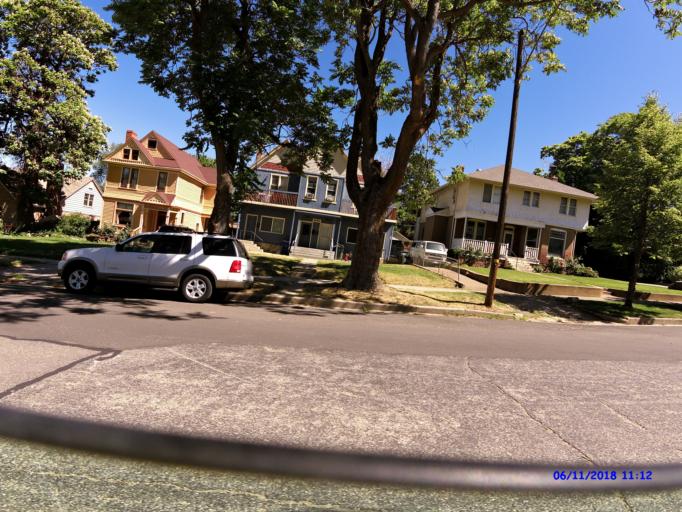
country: US
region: Utah
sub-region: Weber County
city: Ogden
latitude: 41.2202
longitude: -111.9414
